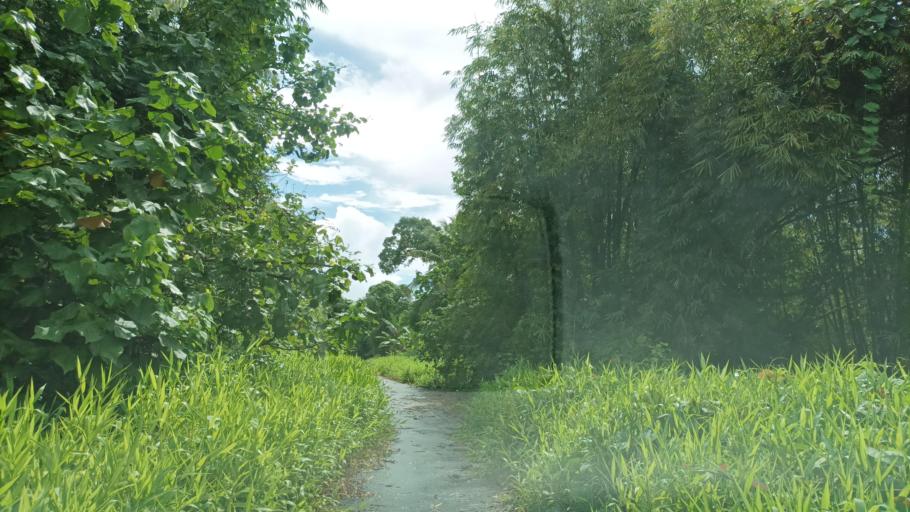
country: FM
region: Pohnpei
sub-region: Madolenihm Municipality
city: Madolenihm Municipality Government
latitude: 6.8731
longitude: 158.3147
